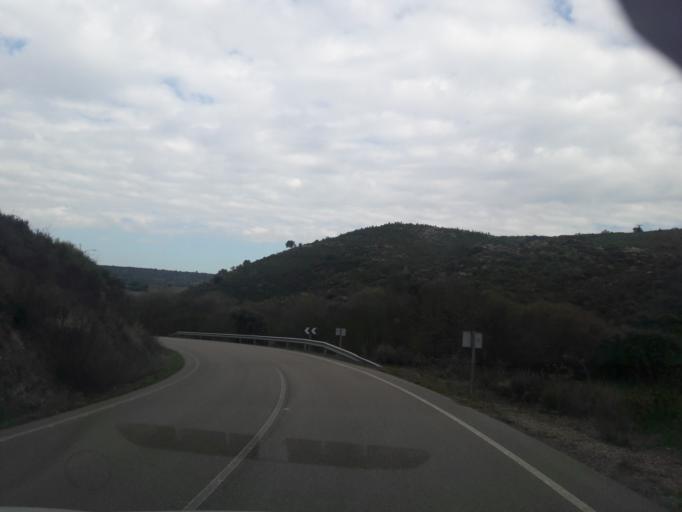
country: ES
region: Castille and Leon
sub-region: Provincia de Salamanca
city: Serradilla del Arroyo
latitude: 40.5145
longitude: -6.3616
